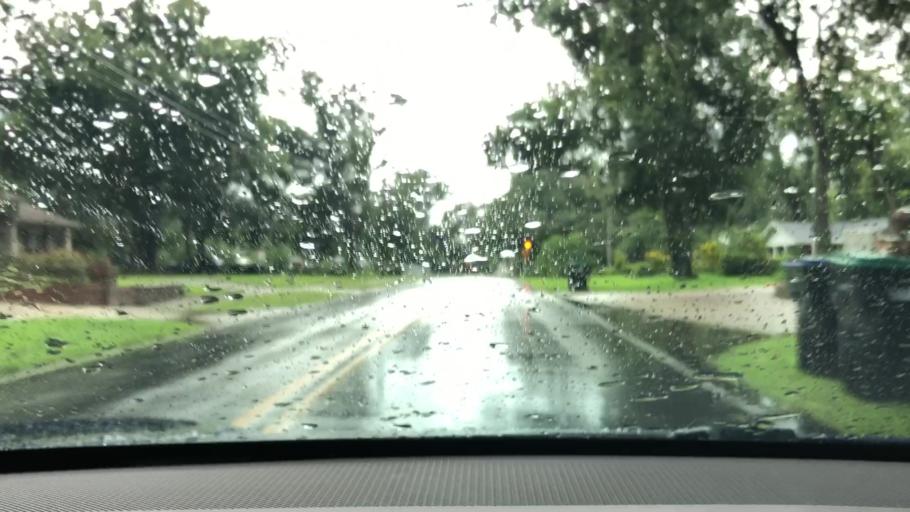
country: US
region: Florida
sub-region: Orange County
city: Edgewood
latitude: 28.4949
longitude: -81.3531
